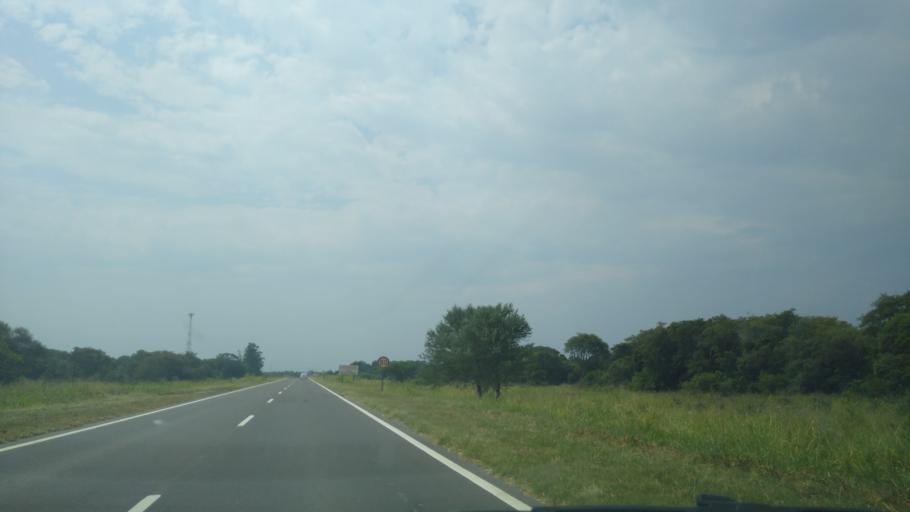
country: AR
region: Chaco
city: Margarita Belen
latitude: -27.0970
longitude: -58.9617
